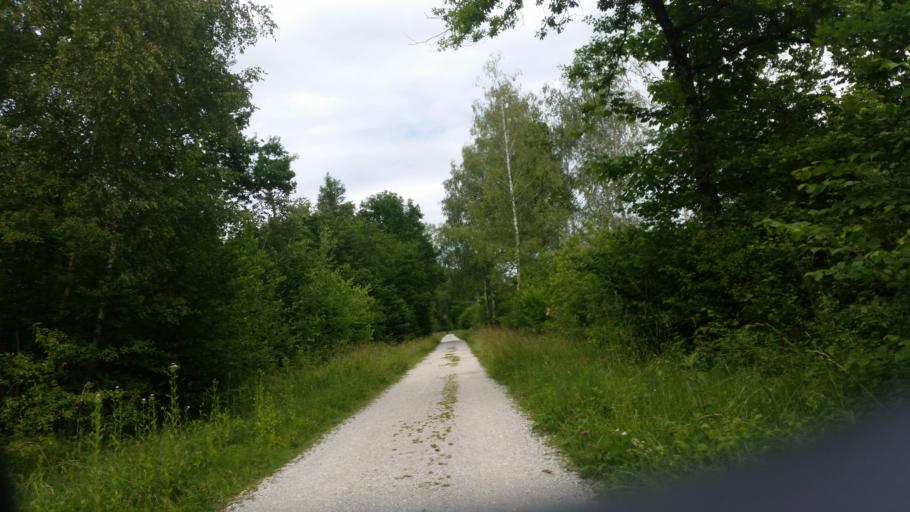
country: CH
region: Vaud
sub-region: Jura-Nord vaudois District
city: Yvonand
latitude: 46.8036
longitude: 6.7649
